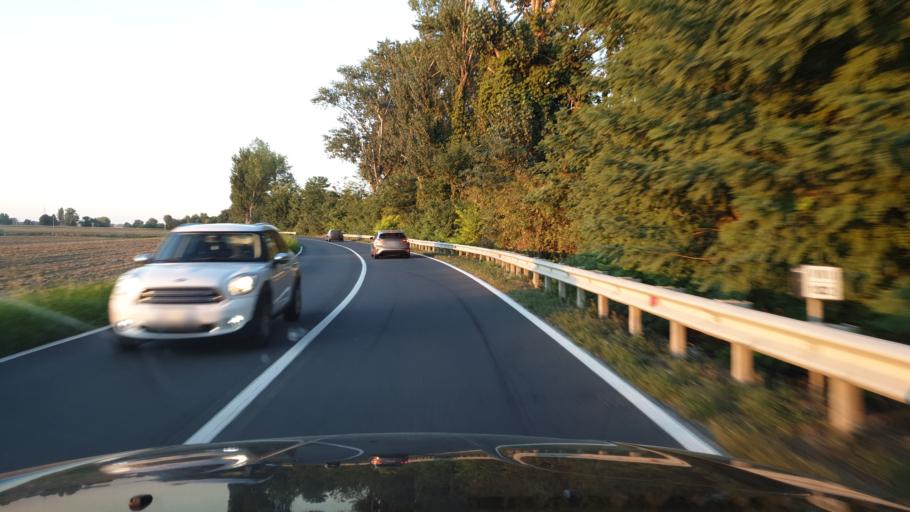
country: IT
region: Emilia-Romagna
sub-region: Provincia di Bologna
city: Progresso
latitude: 44.5562
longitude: 11.3912
